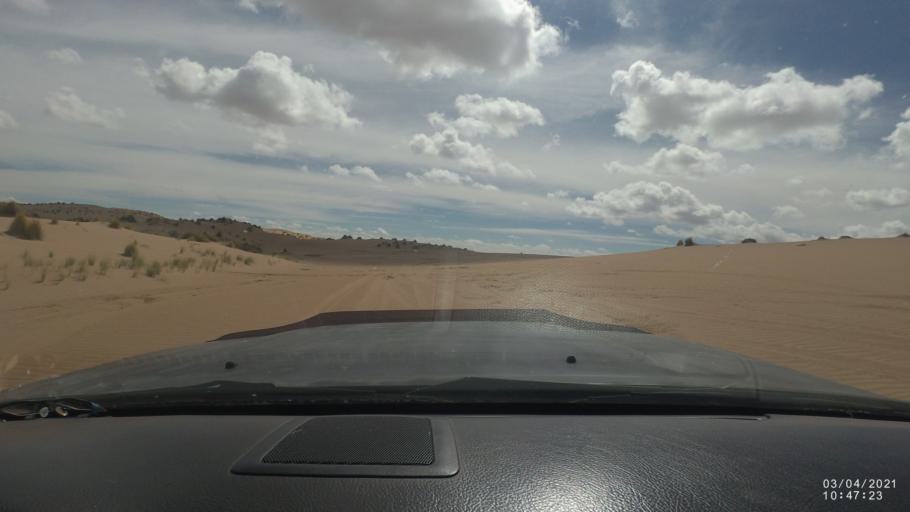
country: BO
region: Oruro
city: Poopo
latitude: -18.7046
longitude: -67.5210
